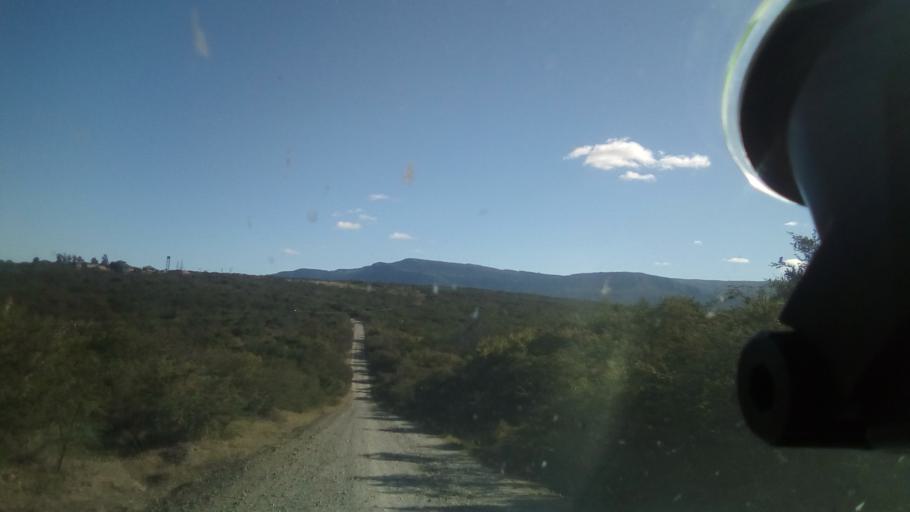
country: ZA
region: Eastern Cape
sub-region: Buffalo City Metropolitan Municipality
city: Bhisho
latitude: -32.7527
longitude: 27.3436
